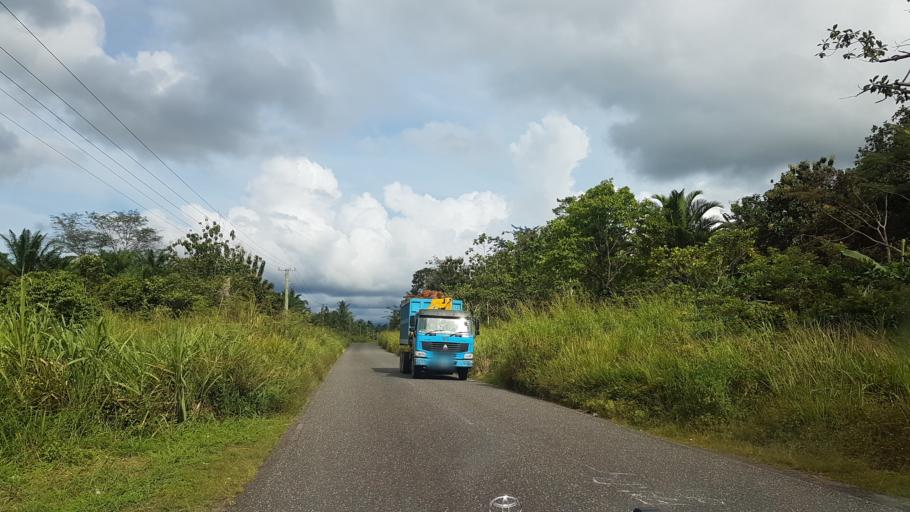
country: PG
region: Northern Province
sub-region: Sohe
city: Popondetta
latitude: -8.8094
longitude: 148.2358
